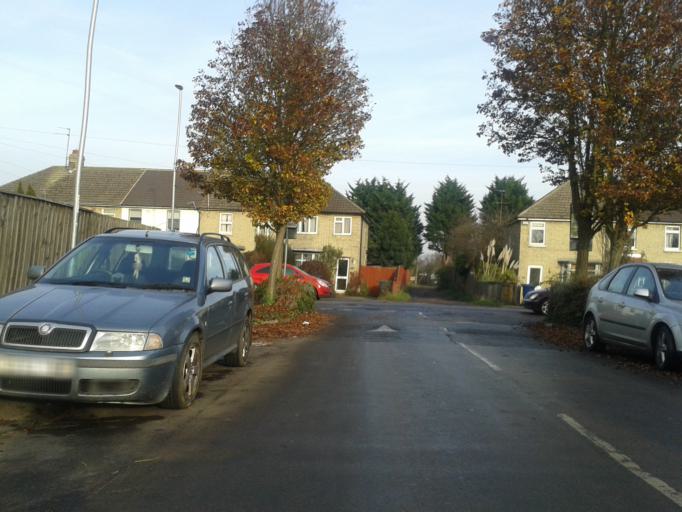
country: GB
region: England
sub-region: Cambridgeshire
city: Cambridge
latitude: 52.2020
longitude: 0.1539
